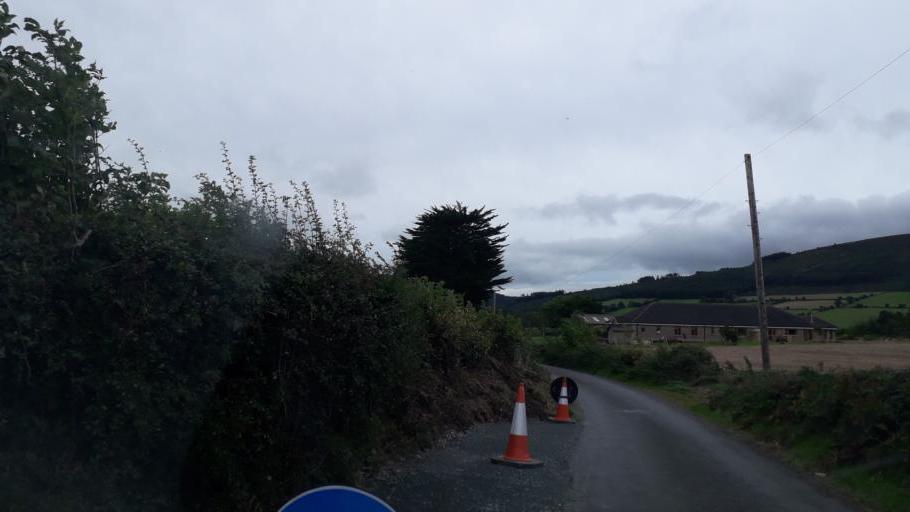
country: IE
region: Leinster
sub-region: Wicklow
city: Enniskerry
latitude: 53.1745
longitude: -6.2031
